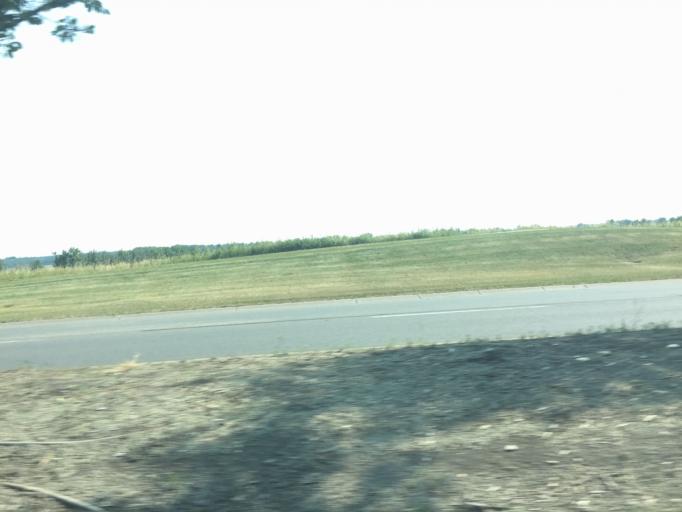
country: CA
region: Alberta
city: Calgary
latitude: 50.9307
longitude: -114.0543
